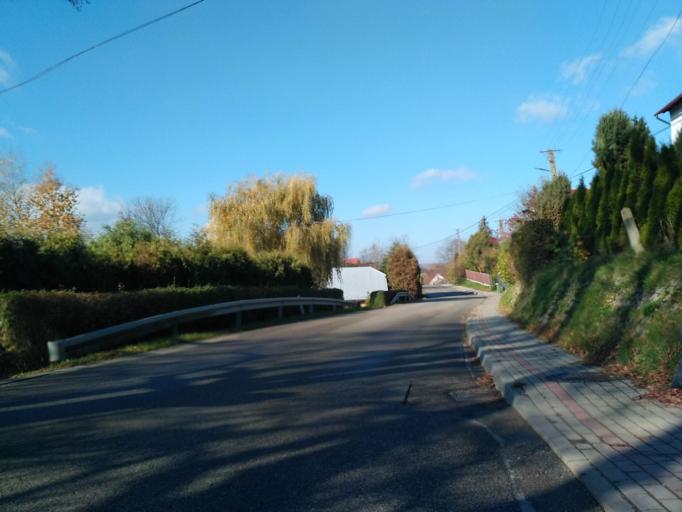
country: PL
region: Subcarpathian Voivodeship
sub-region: Powiat rzeszowski
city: Zglobien
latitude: 50.0246
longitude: 21.8718
